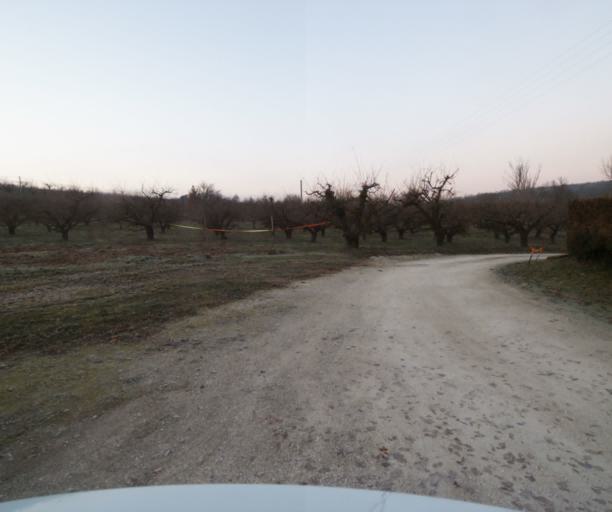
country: FR
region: Midi-Pyrenees
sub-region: Departement du Tarn-et-Garonne
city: Moissac
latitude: 44.1191
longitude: 1.0459
